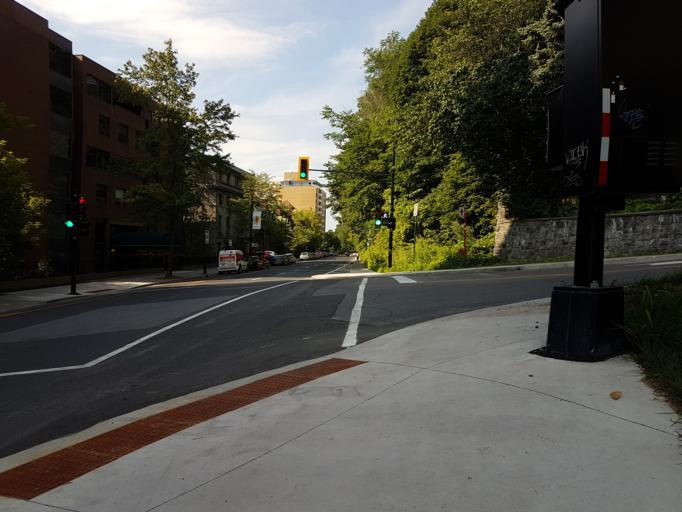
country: CA
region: Quebec
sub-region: Montreal
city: Montreal
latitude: 45.5027
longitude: -73.5837
